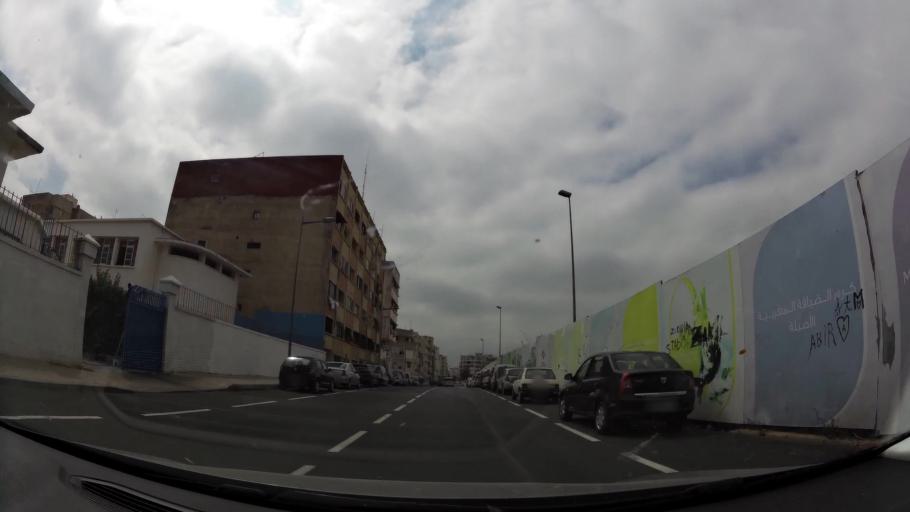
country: MA
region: Rabat-Sale-Zemmour-Zaer
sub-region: Rabat
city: Rabat
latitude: 34.0207
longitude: -6.8531
